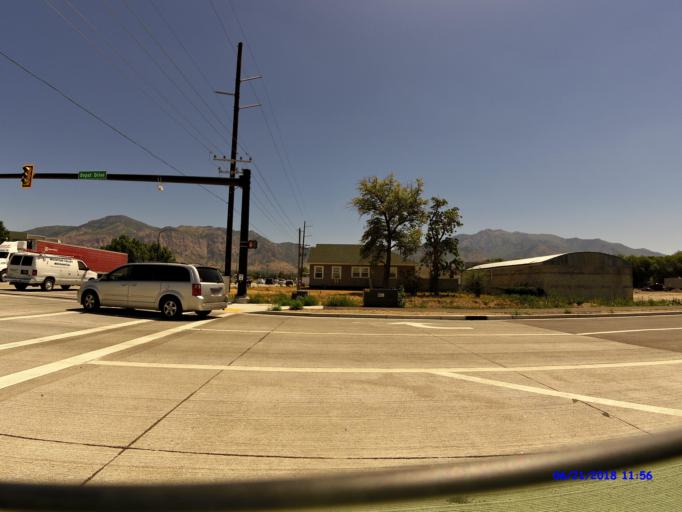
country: US
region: Utah
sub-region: Weber County
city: Ogden
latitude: 41.2442
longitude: -111.9945
